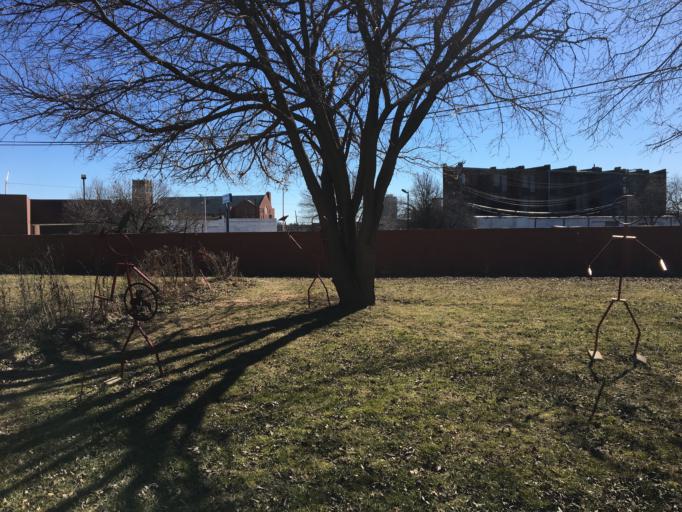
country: US
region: Michigan
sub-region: Wayne County
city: Detroit
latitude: 42.3521
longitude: -83.0337
